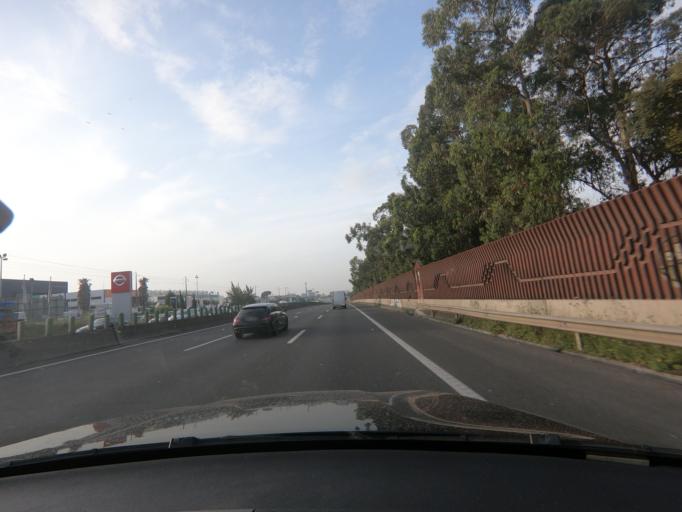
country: PT
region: Setubal
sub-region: Almada
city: Pragal
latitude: 38.6549
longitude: -9.1701
